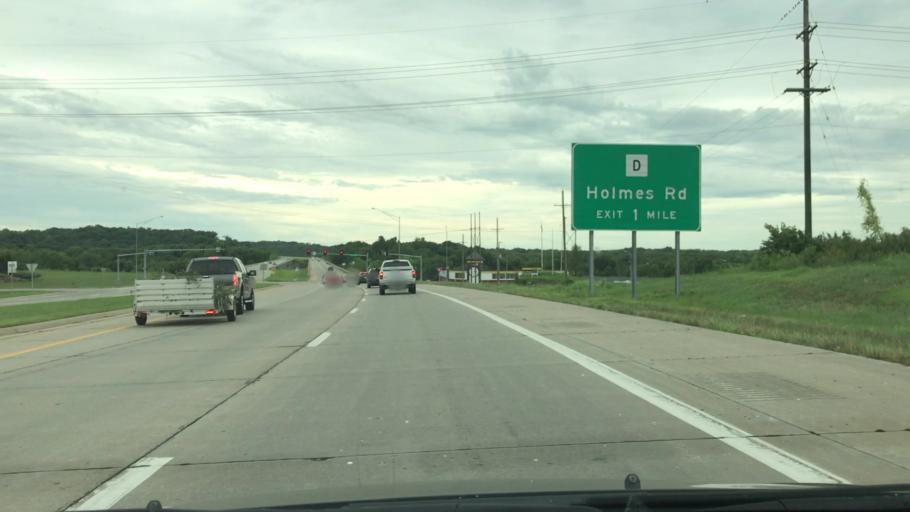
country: US
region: Missouri
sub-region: Jackson County
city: Grandview
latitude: 38.8746
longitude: -94.6036
